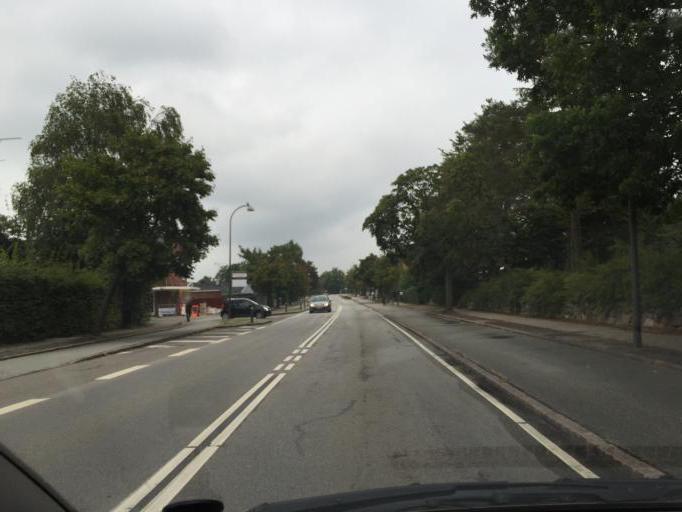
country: DK
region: Capital Region
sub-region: Herlev Kommune
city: Herlev
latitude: 55.7334
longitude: 12.4349
